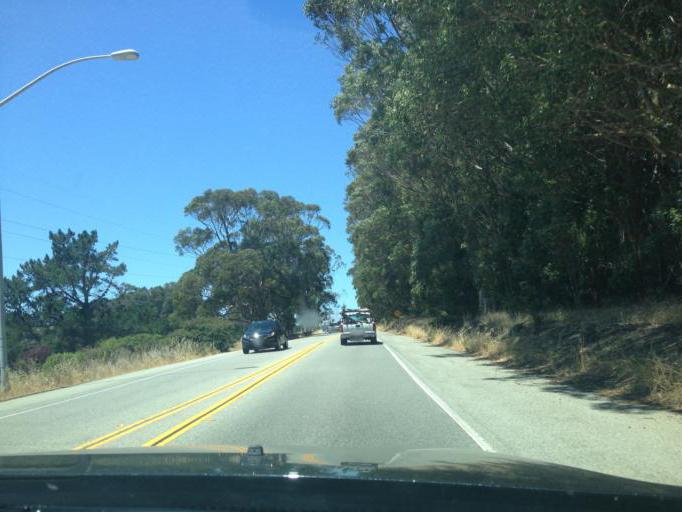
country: US
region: California
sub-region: San Mateo County
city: San Bruno
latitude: 37.6100
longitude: -122.4339
